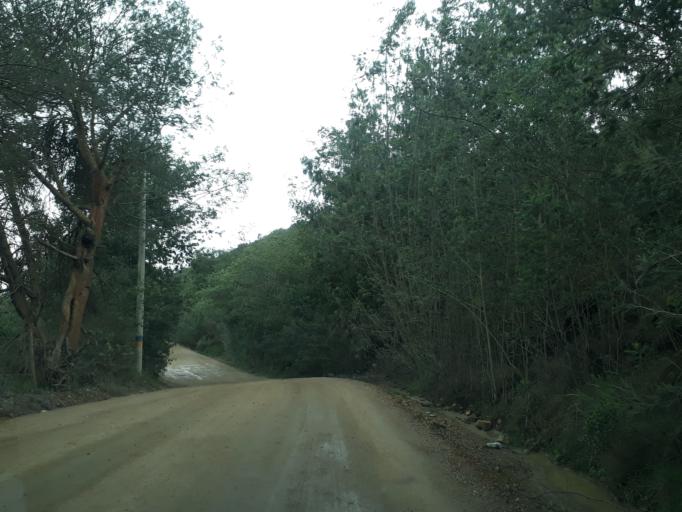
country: CO
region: Cundinamarca
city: Cucunuba
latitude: 5.1937
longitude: -73.7816
